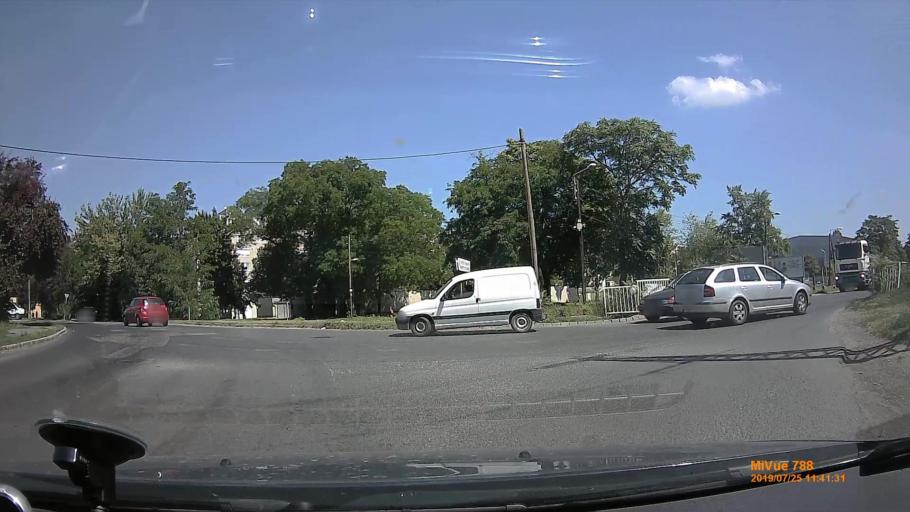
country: HU
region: Szabolcs-Szatmar-Bereg
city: Nyiregyhaza
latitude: 47.9410
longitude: 21.7137
